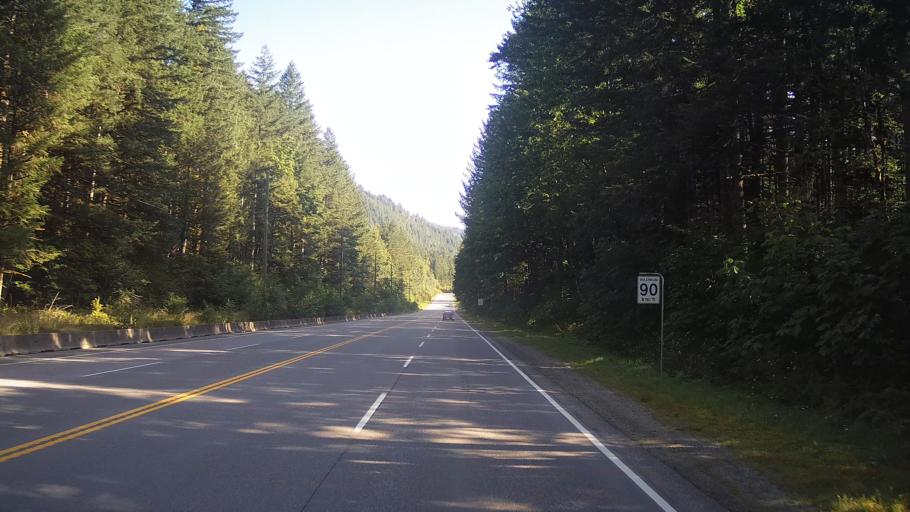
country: CA
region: British Columbia
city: Hope
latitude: 49.4534
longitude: -121.4367
